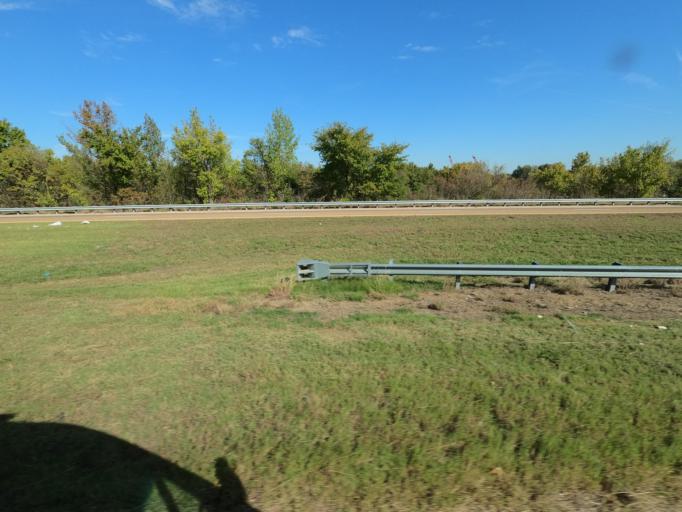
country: US
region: Tennessee
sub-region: Shelby County
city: Millington
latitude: 35.3302
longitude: -89.8999
